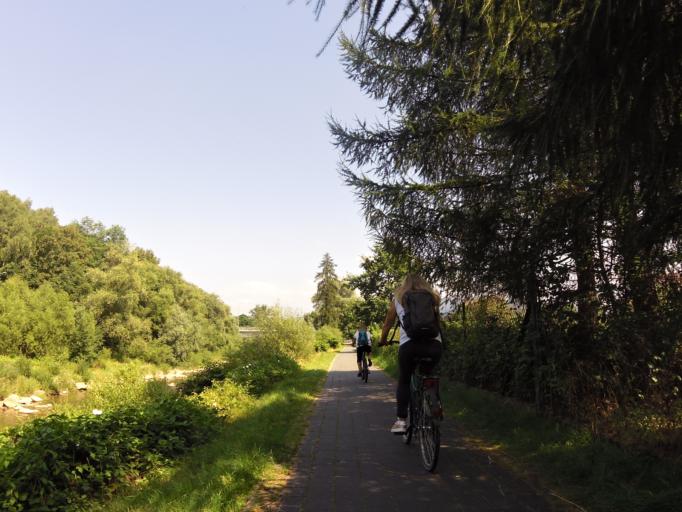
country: PL
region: Silesian Voivodeship
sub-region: Powiat zywiecki
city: Wegierska Gorka
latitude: 49.6089
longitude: 19.1137
